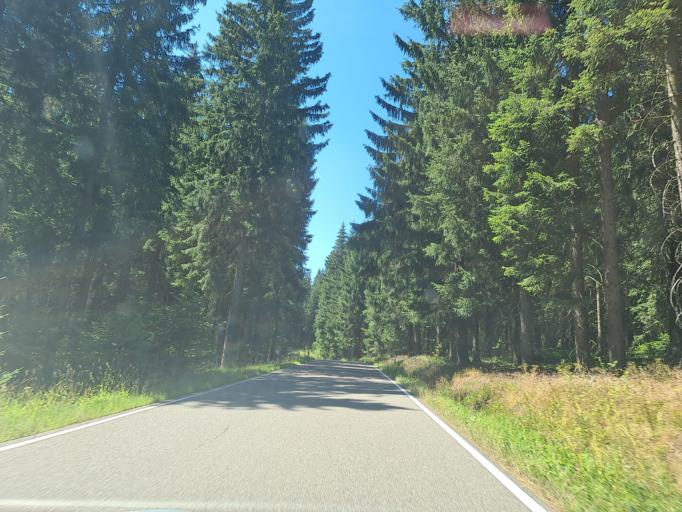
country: DE
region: Saxony
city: Rechenberg-Bienenmuhle
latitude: 50.7154
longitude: 13.5362
